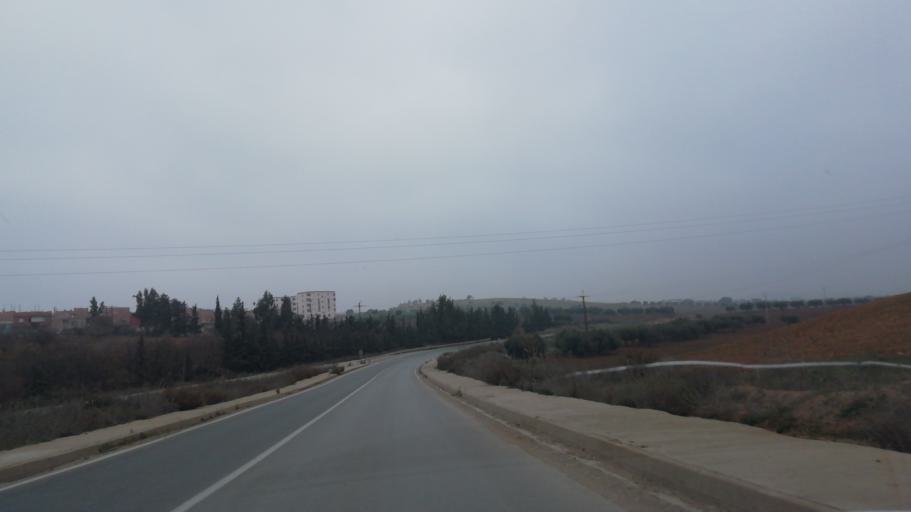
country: DZ
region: Mascara
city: Mascara
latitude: 35.4162
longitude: 0.1213
